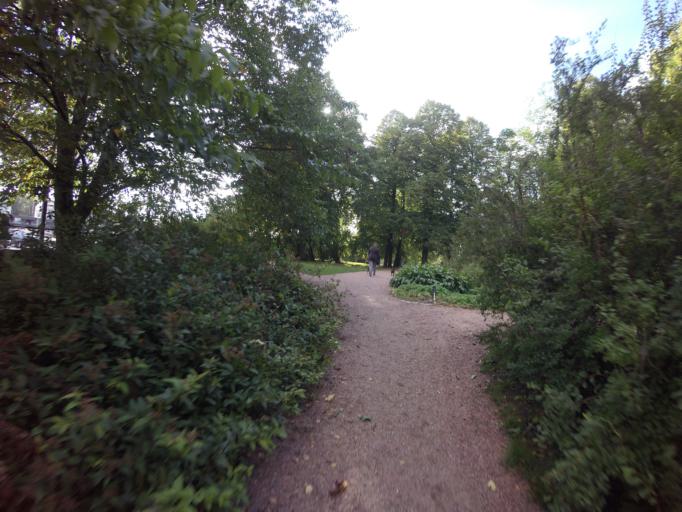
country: FI
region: Varsinais-Suomi
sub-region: Turku
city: Turku
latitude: 60.4353
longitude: 22.2312
